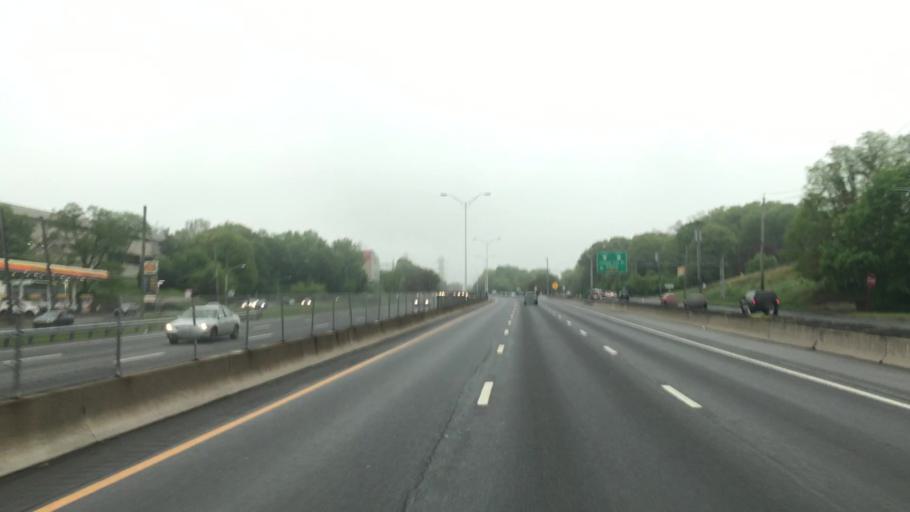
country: US
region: New York
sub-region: Westchester County
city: Bronxville
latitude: 40.9351
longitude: -73.8560
